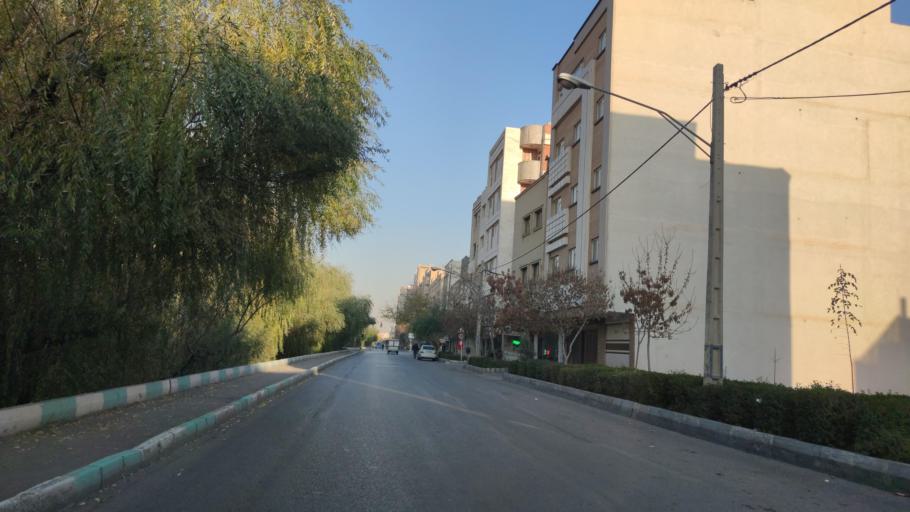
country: IR
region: Isfahan
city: Isfahan
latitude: 32.7089
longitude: 51.6847
